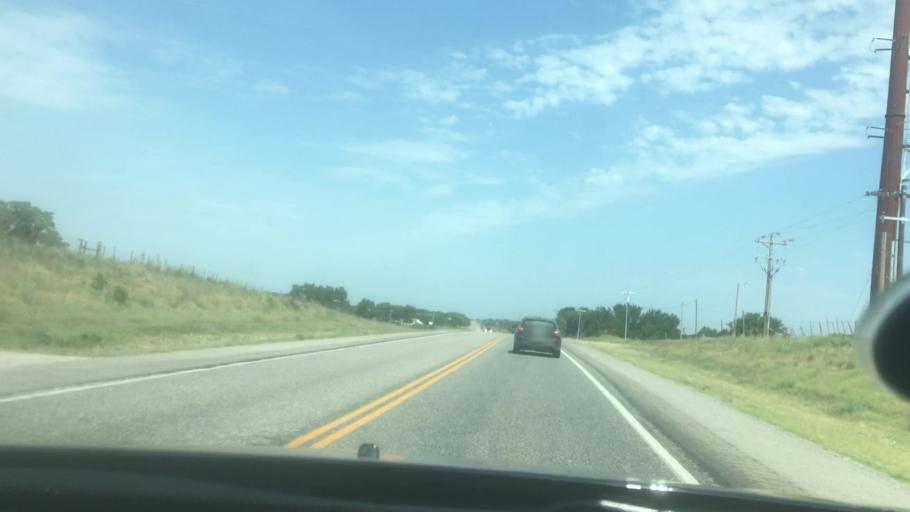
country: US
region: Oklahoma
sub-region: Seminole County
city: Konawa
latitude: 34.8670
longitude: -96.8338
